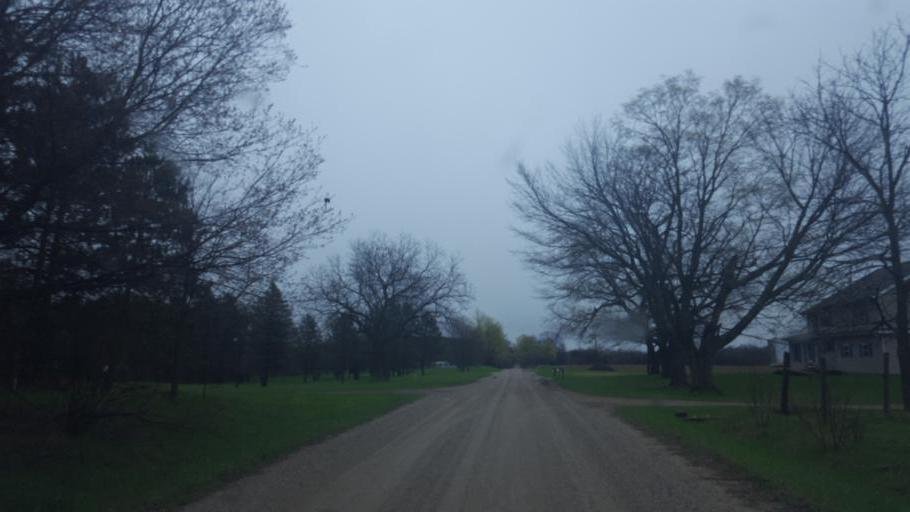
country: US
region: Michigan
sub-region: Isabella County
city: Lake Isabella
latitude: 43.5672
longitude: -85.0166
